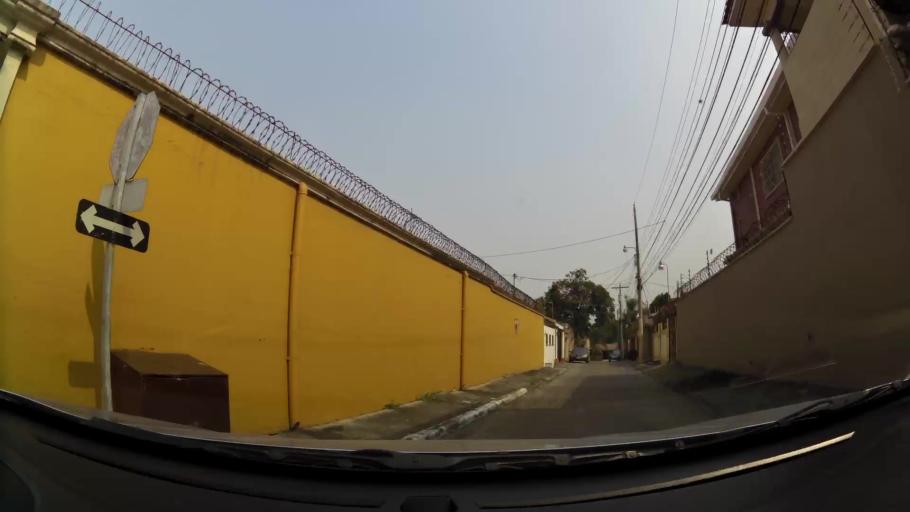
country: HN
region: Cortes
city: Armenta
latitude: 15.4962
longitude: -88.0408
